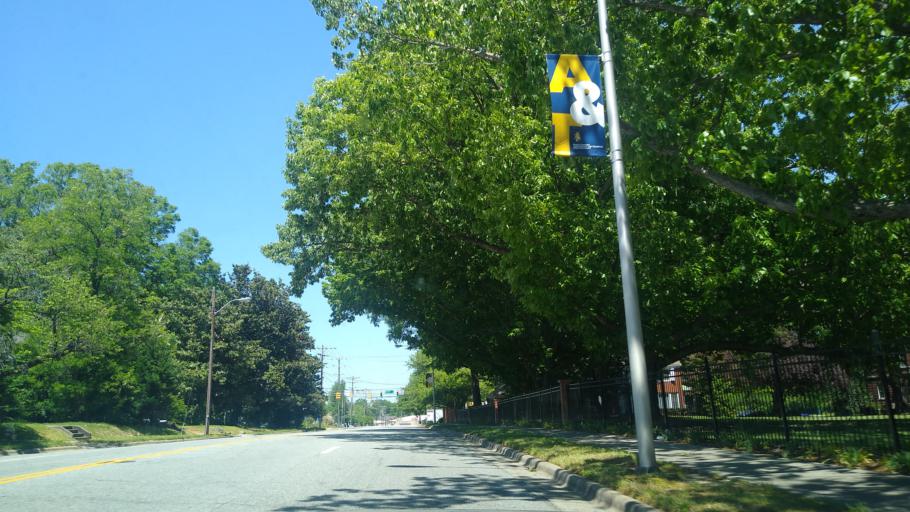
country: US
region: North Carolina
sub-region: Guilford County
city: Greensboro
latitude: 36.0744
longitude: -79.7786
